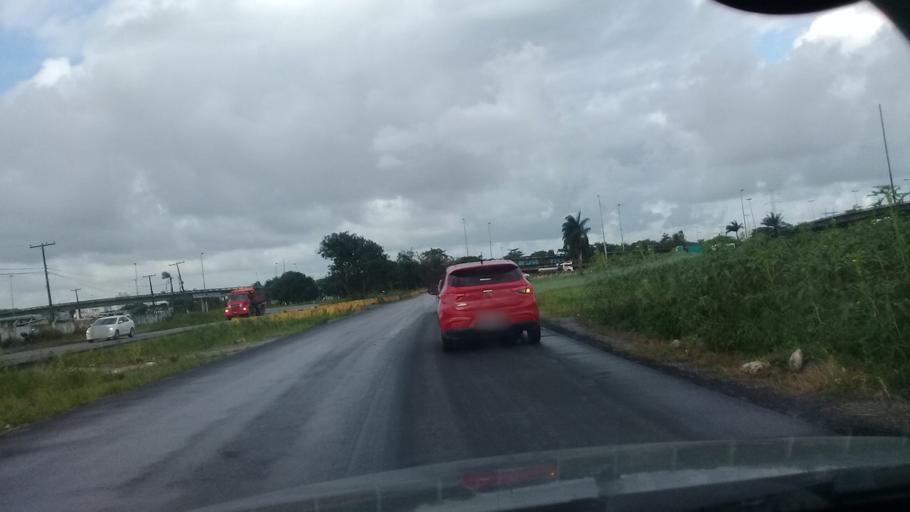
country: BR
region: Pernambuco
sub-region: Recife
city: Recife
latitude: -8.0665
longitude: -34.9456
